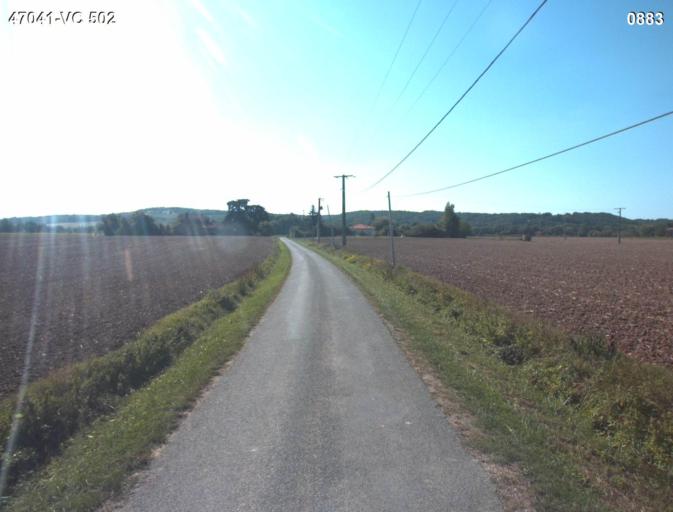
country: FR
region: Aquitaine
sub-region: Departement du Lot-et-Garonne
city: Port-Sainte-Marie
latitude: 44.2247
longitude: 0.3940
